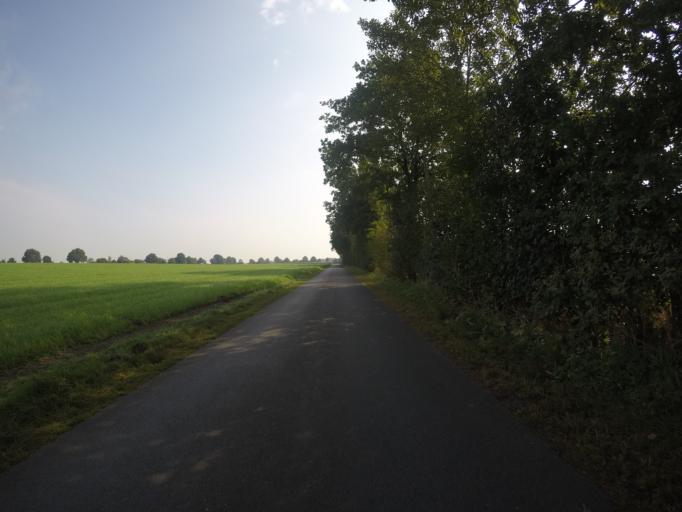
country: DE
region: North Rhine-Westphalia
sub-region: Regierungsbezirk Munster
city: Isselburg
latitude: 51.8300
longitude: 6.5218
